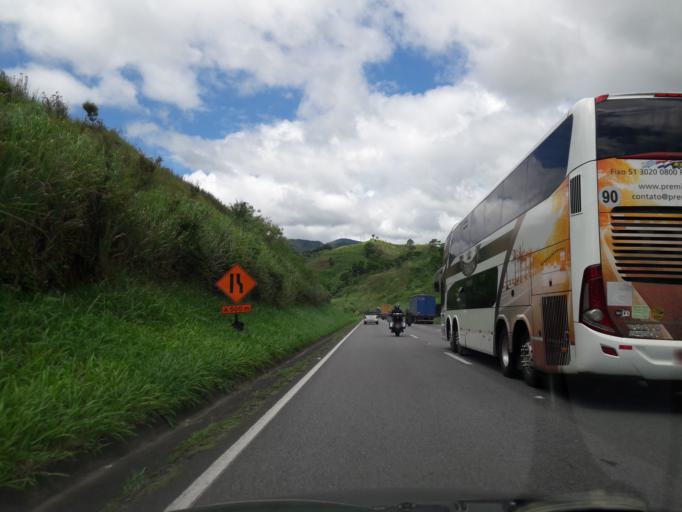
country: BR
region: Sao Paulo
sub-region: Cajati
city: Cajati
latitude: -24.8301
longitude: -48.2201
